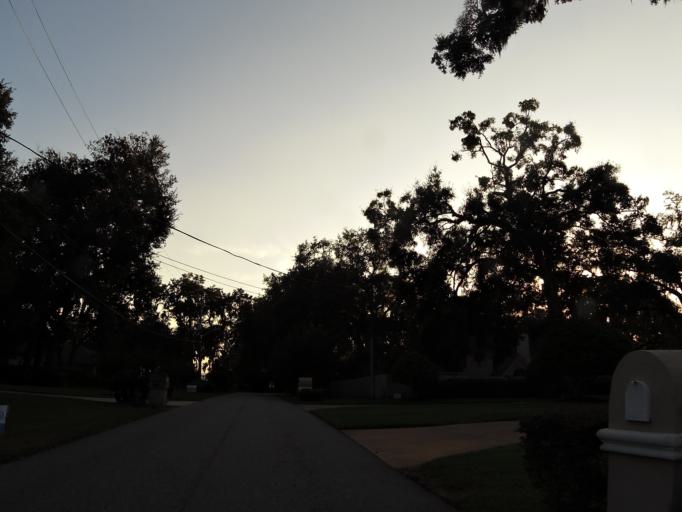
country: US
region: Florida
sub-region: Clay County
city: Orange Park
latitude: 30.2004
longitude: -81.6391
